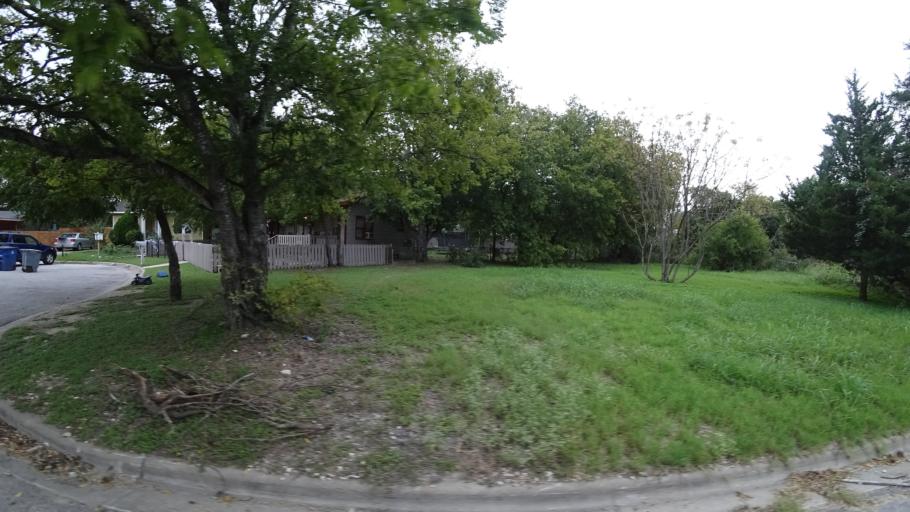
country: US
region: Texas
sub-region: Travis County
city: Austin
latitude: 30.2724
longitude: -97.6943
